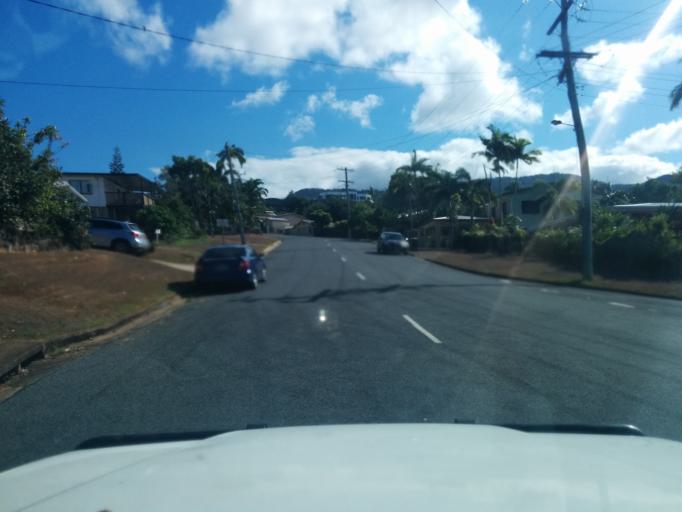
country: AU
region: Queensland
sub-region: Cairns
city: Woree
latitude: -16.9494
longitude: 145.7332
